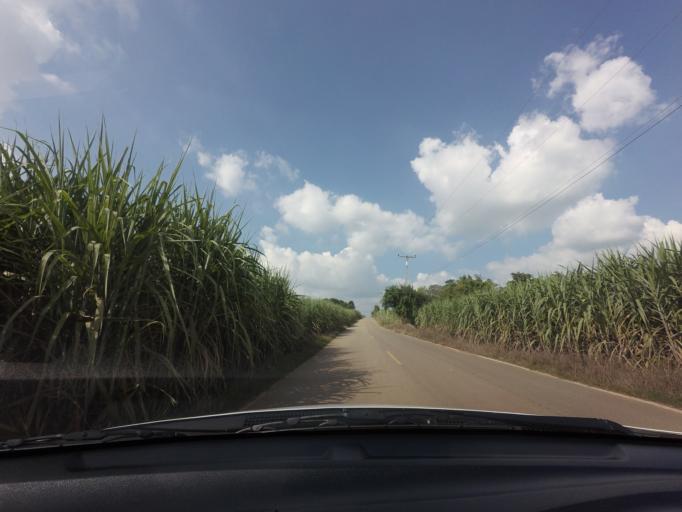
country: TH
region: Nakhon Ratchasima
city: Wang Nam Khiao
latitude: 14.5097
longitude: 101.6302
